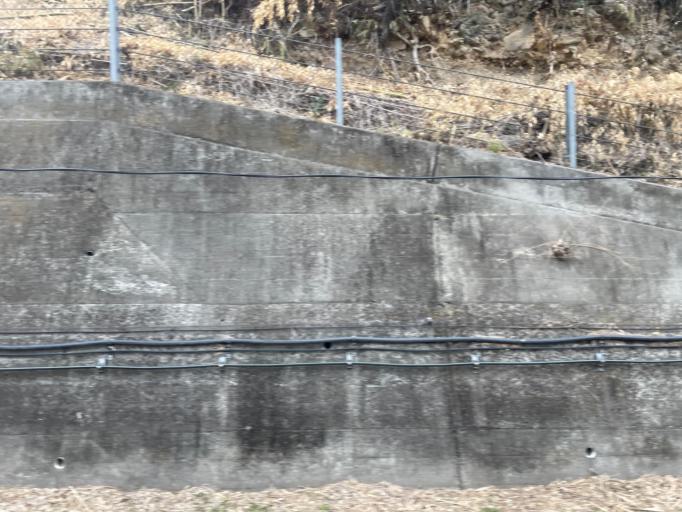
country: JP
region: Gunma
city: Numata
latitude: 36.5720
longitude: 139.0510
